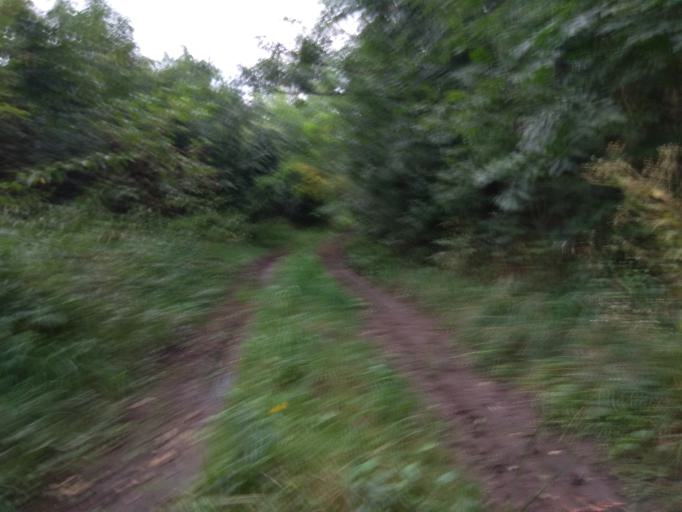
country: HU
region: Borsod-Abauj-Zemplen
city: Megyaszo
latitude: 48.1467
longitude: 21.0814
